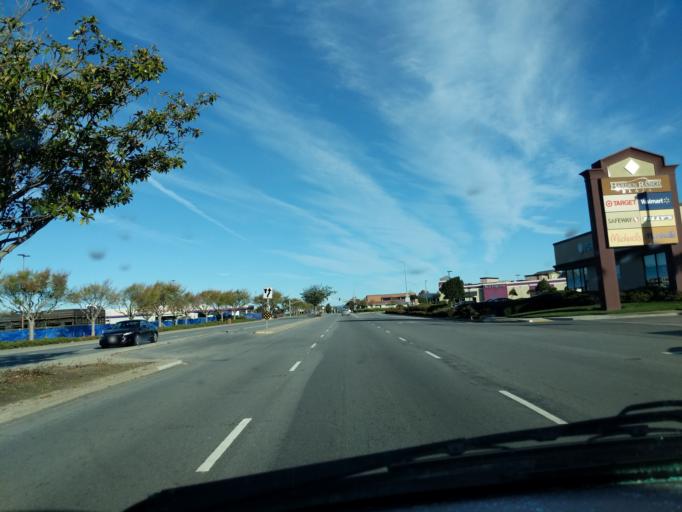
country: US
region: California
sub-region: Monterey County
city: Boronda
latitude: 36.7149
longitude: -121.6549
